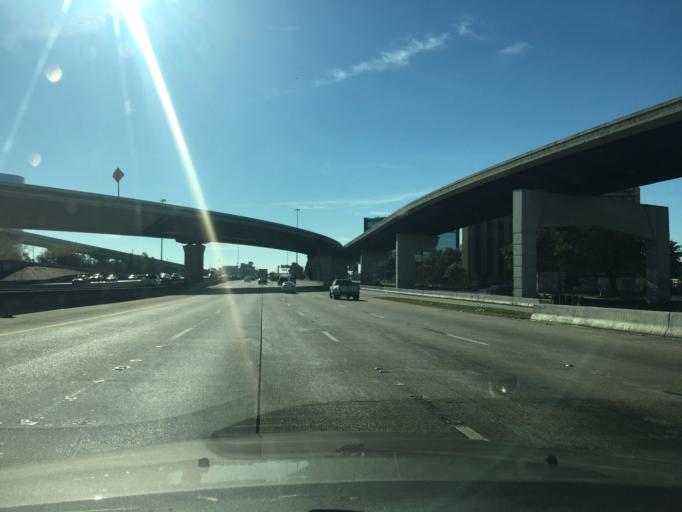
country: US
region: Texas
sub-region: Harris County
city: Aldine
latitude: 29.9393
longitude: -95.4137
